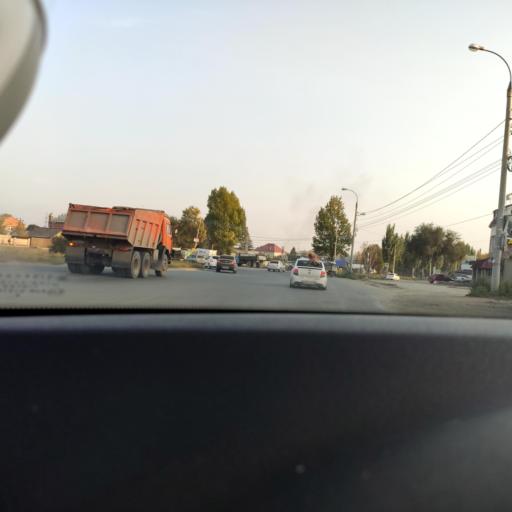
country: RU
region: Samara
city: Petra-Dubrava
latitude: 53.2538
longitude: 50.3093
